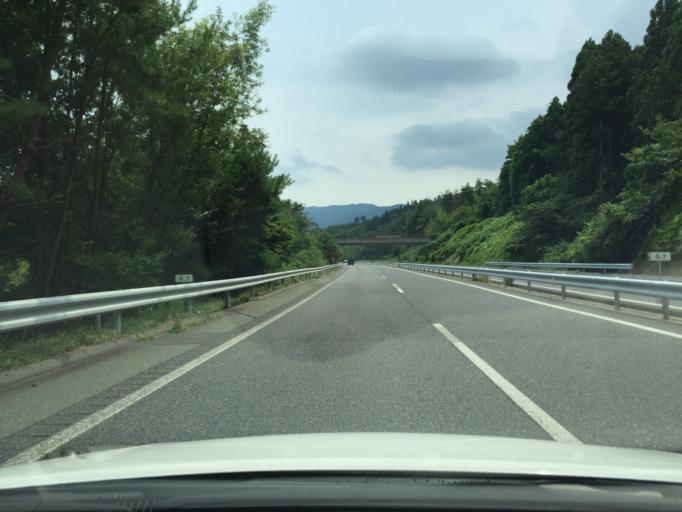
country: JP
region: Fukushima
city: Iwaki
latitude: 37.0737
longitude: 140.7914
